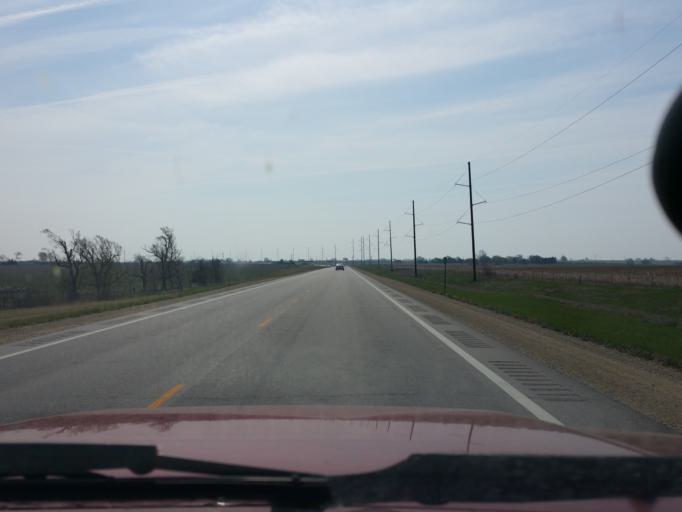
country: US
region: Kansas
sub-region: Riley County
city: Ogden
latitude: 39.2841
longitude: -96.7439
